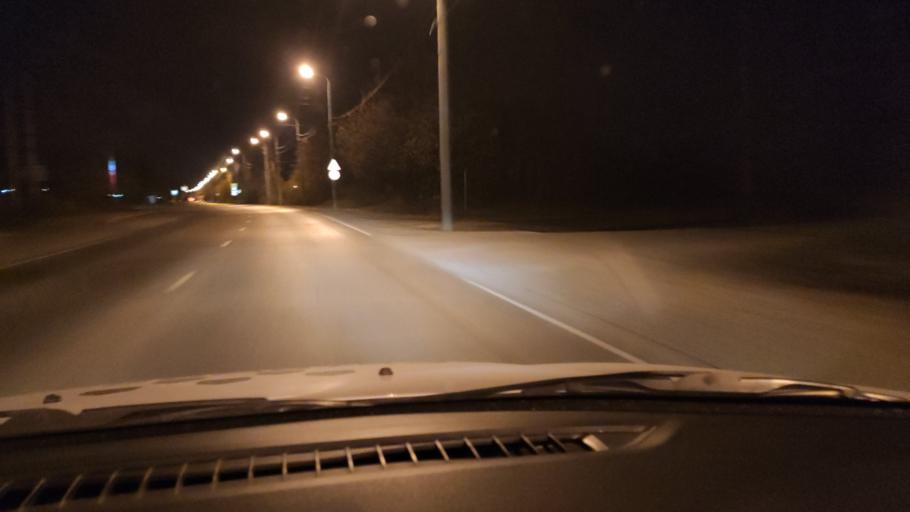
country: RU
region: Perm
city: Kondratovo
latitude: 57.9725
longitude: 56.1280
